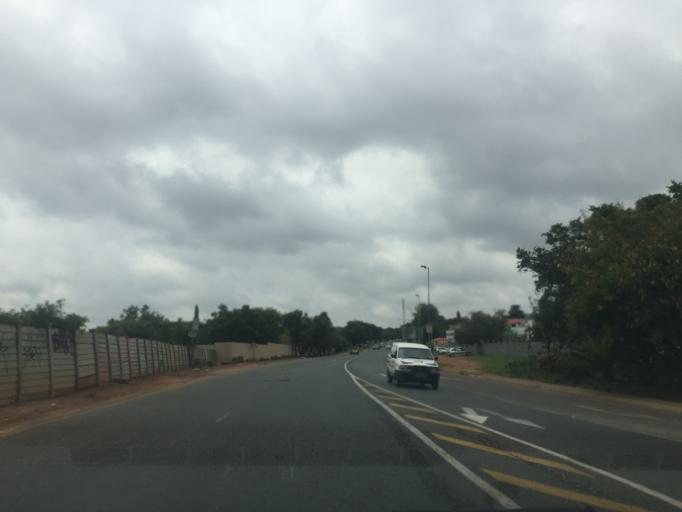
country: ZA
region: Gauteng
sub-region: City of Johannesburg Metropolitan Municipality
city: Johannesburg
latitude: -26.1106
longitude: 27.9902
